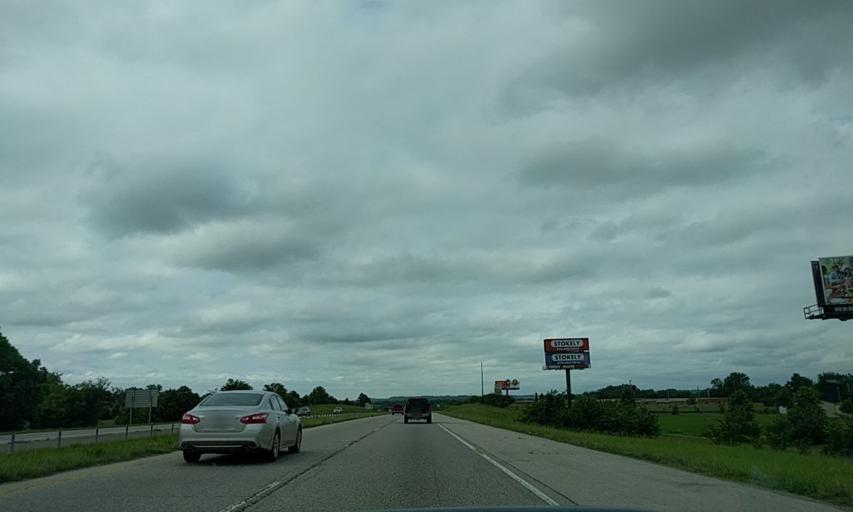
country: US
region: Oklahoma
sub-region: Tulsa County
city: Jenks
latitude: 36.0374
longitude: -96.0087
